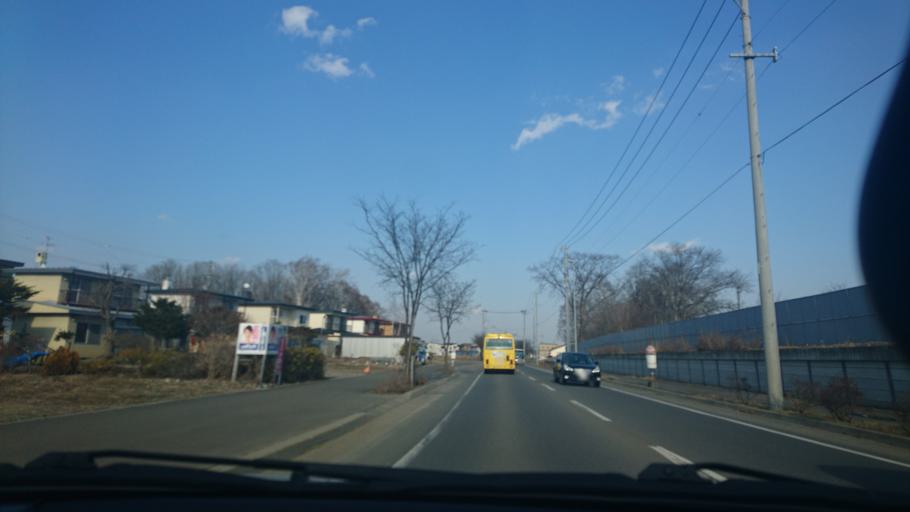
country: JP
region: Hokkaido
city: Obihiro
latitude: 42.9240
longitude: 143.1788
